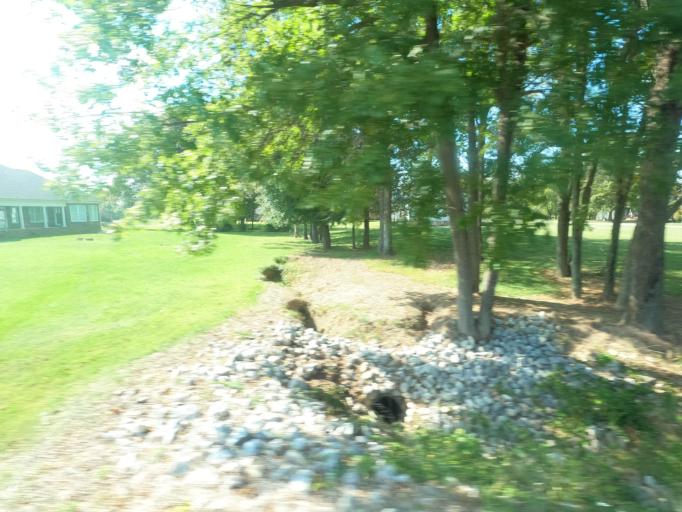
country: US
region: Illinois
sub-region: Massac County
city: Metropolis
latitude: 37.2012
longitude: -88.7292
